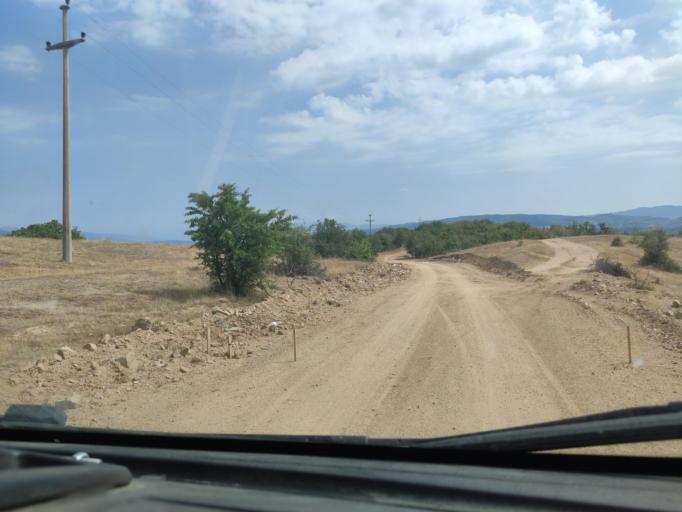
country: MK
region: Radovis
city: Radovish
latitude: 41.6675
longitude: 22.4067
